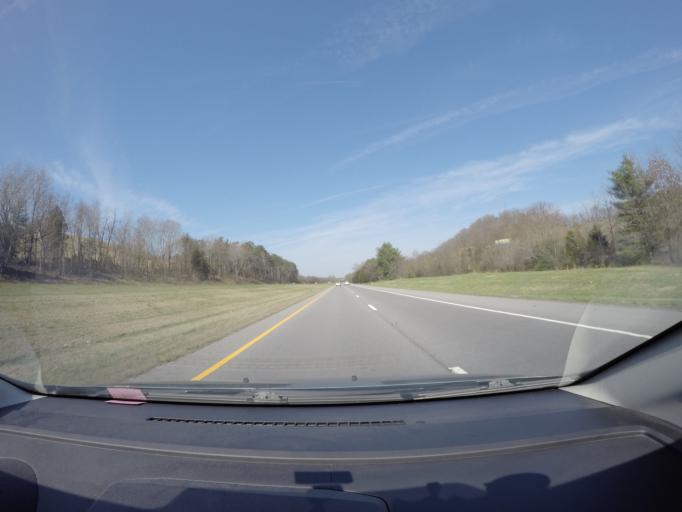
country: US
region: Tennessee
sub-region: Coffee County
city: New Union
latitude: 35.5652
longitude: -86.2166
